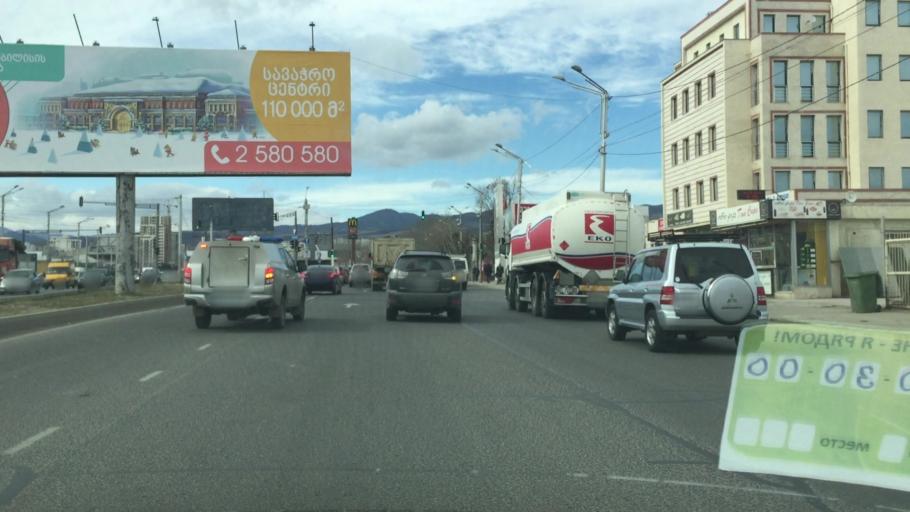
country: GE
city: Zahesi
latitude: 41.7869
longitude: 44.7801
